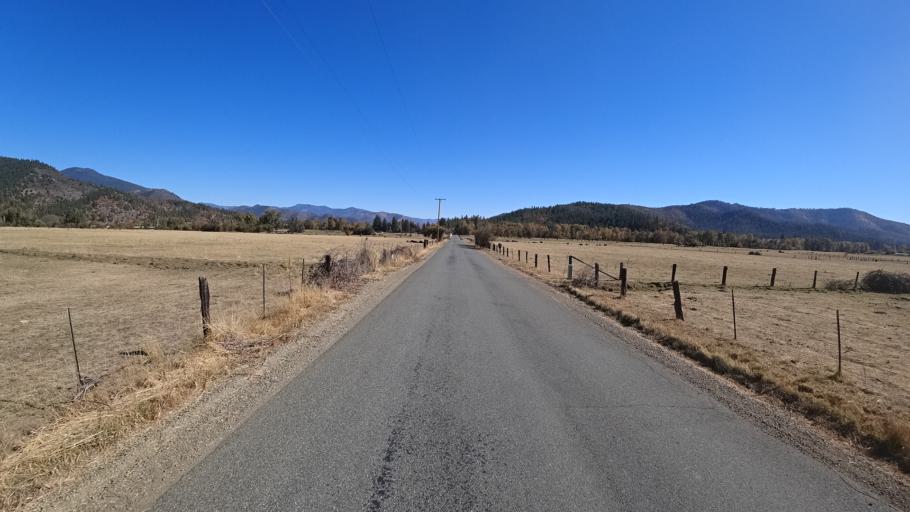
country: US
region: California
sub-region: Siskiyou County
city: Yreka
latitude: 41.6240
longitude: -122.9747
